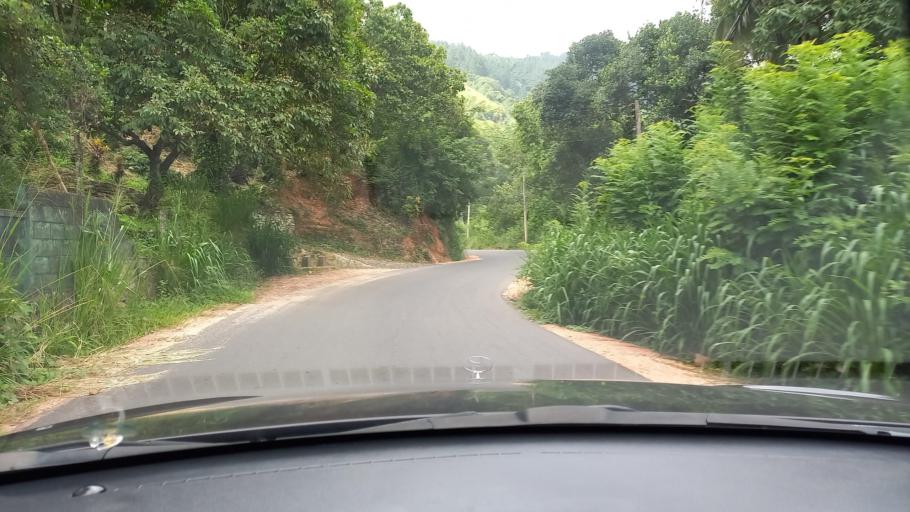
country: LK
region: Central
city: Gampola
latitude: 7.2044
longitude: 80.6268
